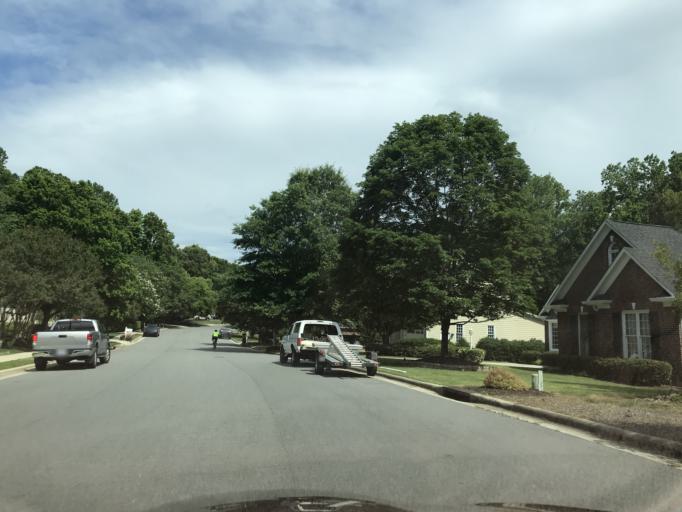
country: US
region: North Carolina
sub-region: Wake County
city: West Raleigh
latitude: 35.8833
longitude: -78.6859
